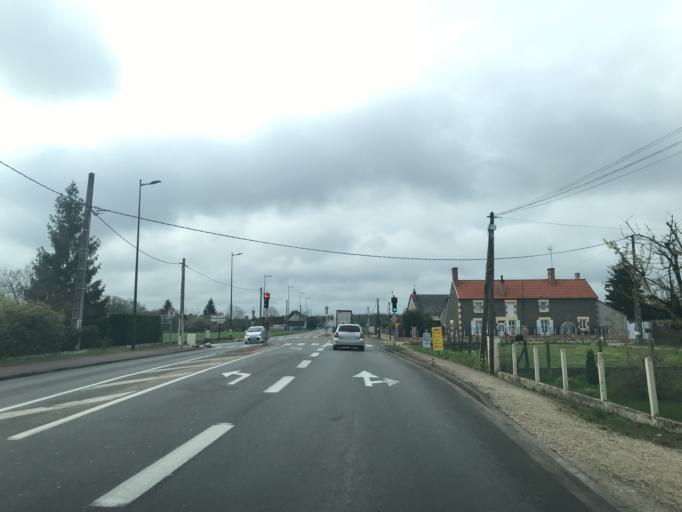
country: FR
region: Centre
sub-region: Departement du Loiret
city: Bray-en-Val
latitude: 47.8312
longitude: 2.3680
